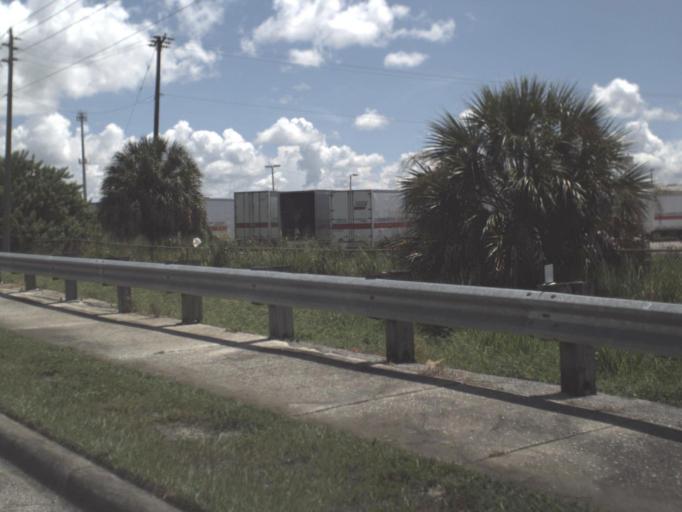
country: US
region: Florida
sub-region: Polk County
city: Auburndale
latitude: 28.0599
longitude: -81.7989
